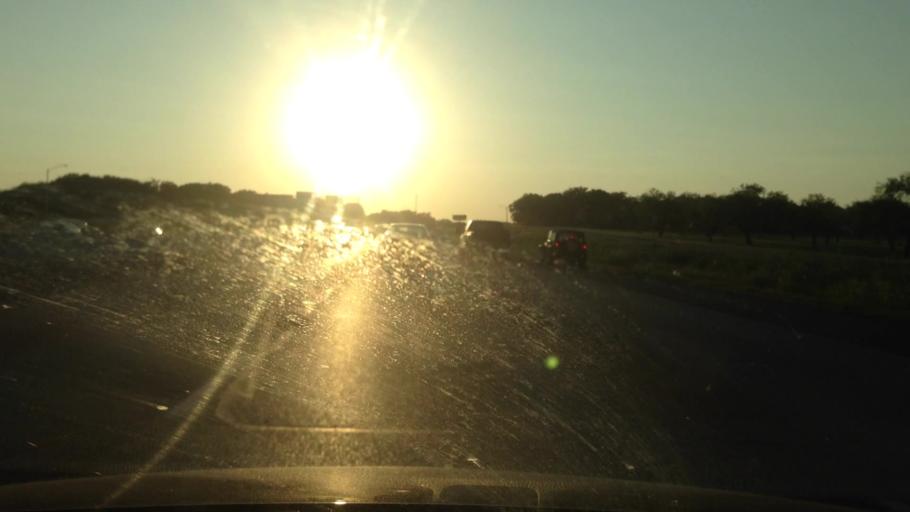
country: US
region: Texas
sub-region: Tarrant County
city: Forest Hill
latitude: 32.6950
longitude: -97.2526
